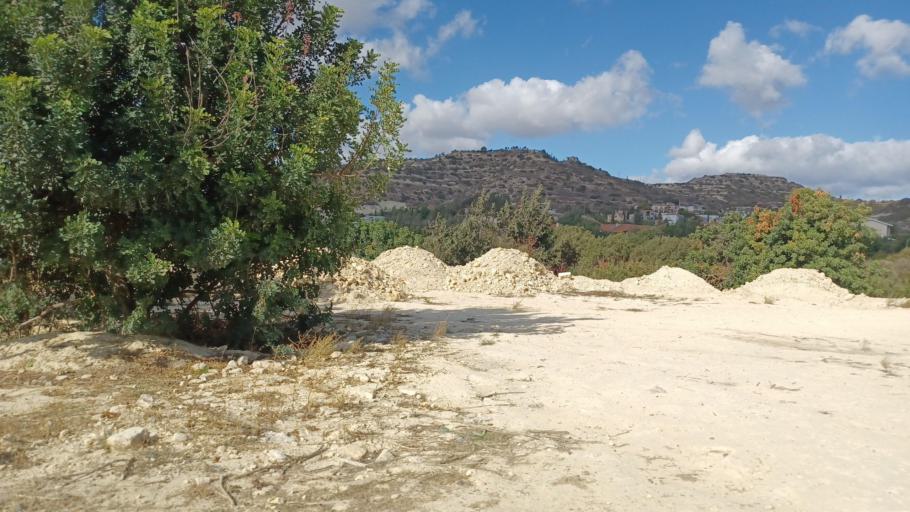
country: CY
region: Limassol
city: Pano Polemidia
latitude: 34.7422
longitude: 32.9988
